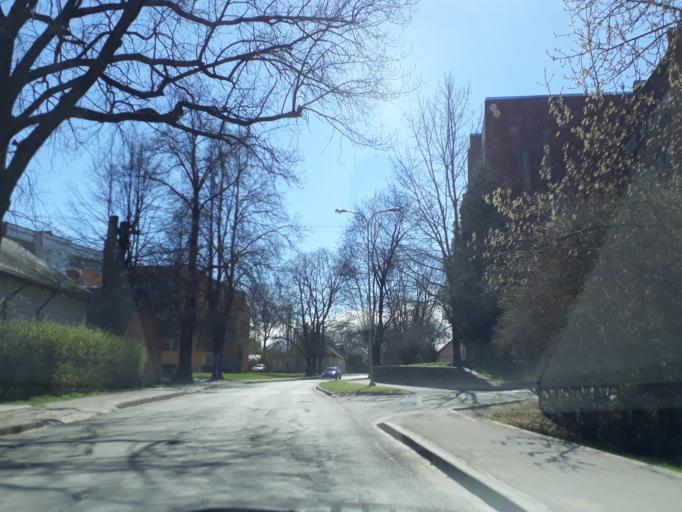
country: LV
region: Dobeles Rajons
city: Dobele
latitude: 56.6187
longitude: 23.2816
